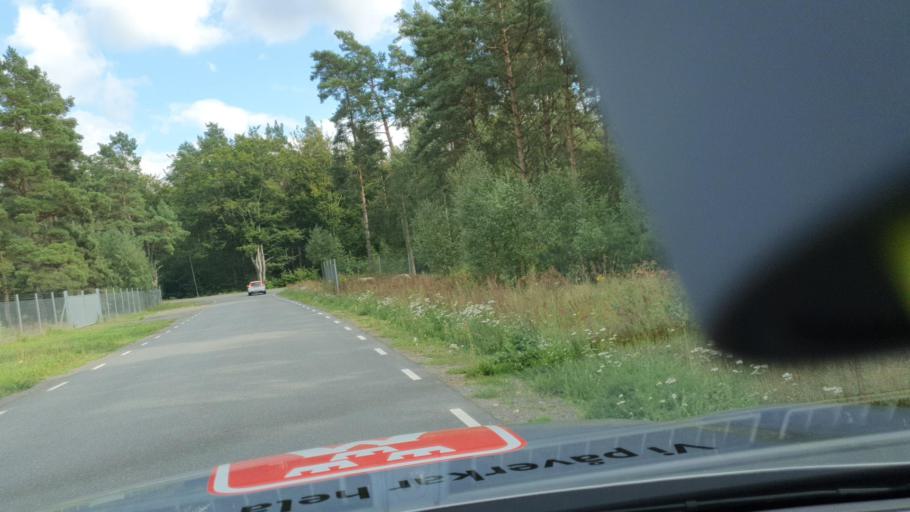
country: SE
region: Skane
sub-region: Kristianstads Kommun
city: Norra Asum
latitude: 55.9861
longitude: 14.1322
